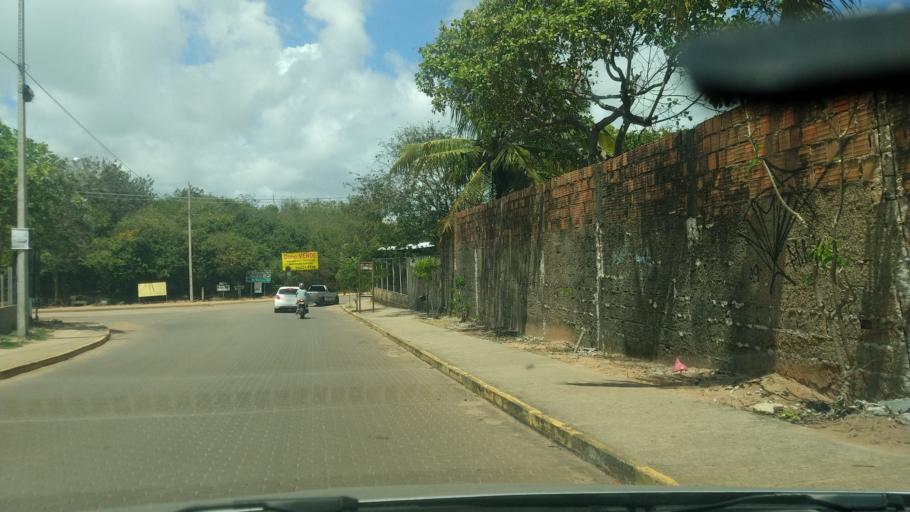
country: BR
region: Rio Grande do Norte
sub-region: Ares
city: Ares
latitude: -6.2342
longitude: -35.0490
